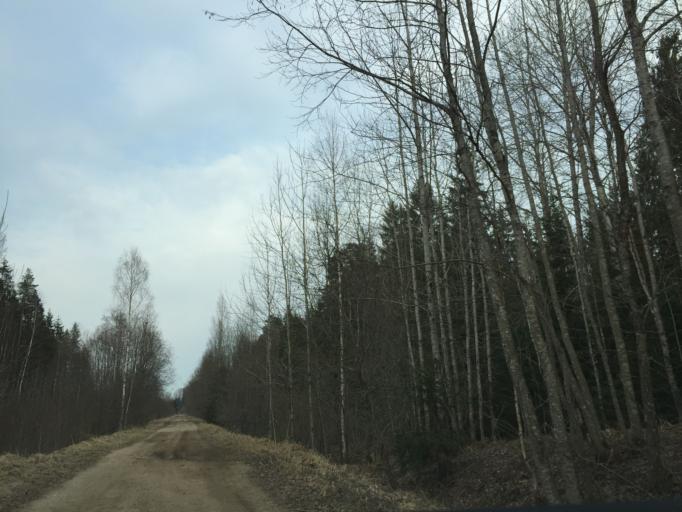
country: LV
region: Amatas Novads
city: Drabesi
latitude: 57.1996
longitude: 25.3780
